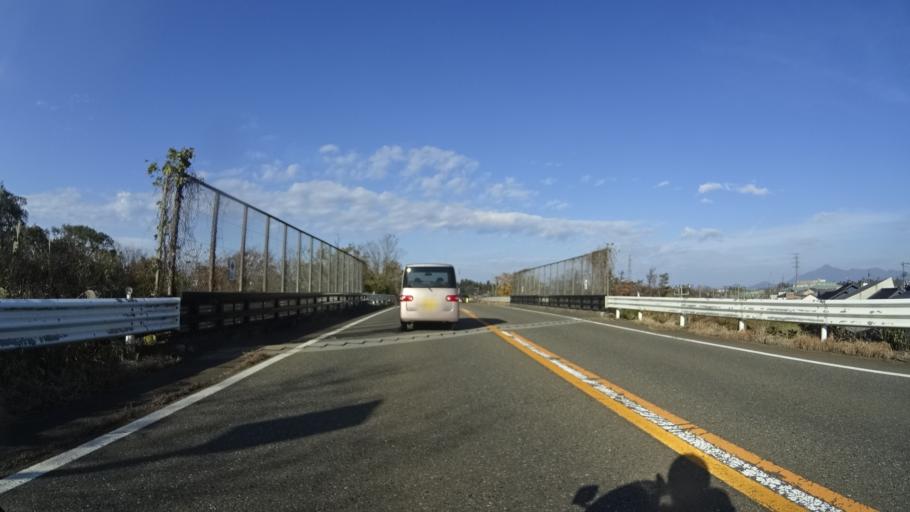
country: JP
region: Niigata
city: Joetsu
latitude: 37.2069
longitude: 138.3002
